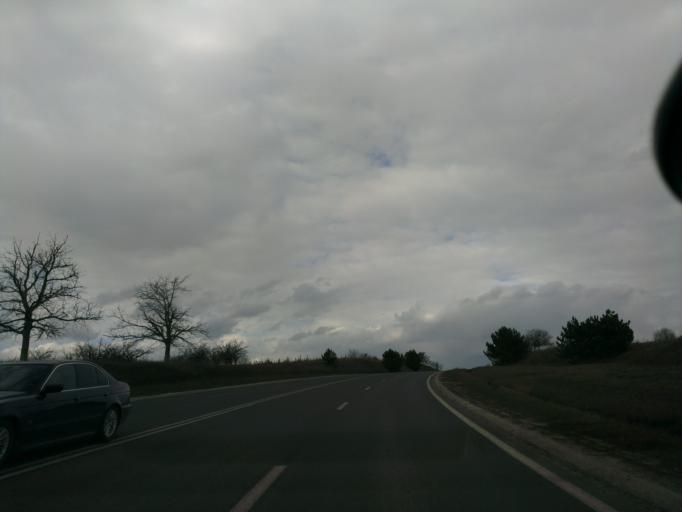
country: MD
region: Laloveni
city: Ialoveni
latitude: 46.9210
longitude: 28.6919
